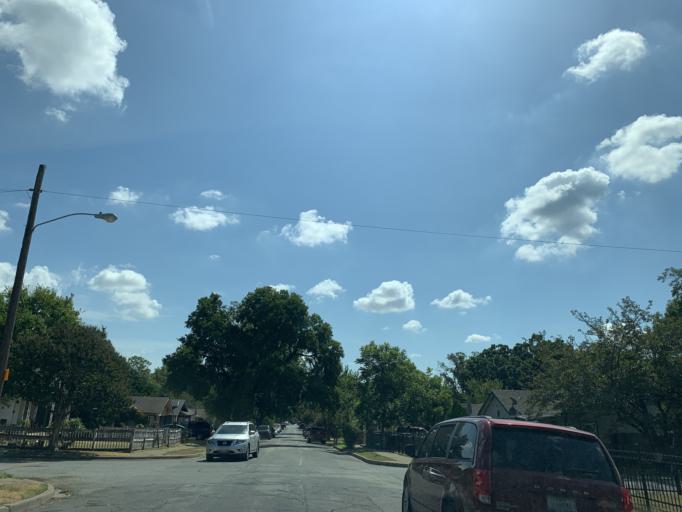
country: US
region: Texas
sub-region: Dallas County
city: Cockrell Hill
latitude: 32.7330
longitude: -96.8617
